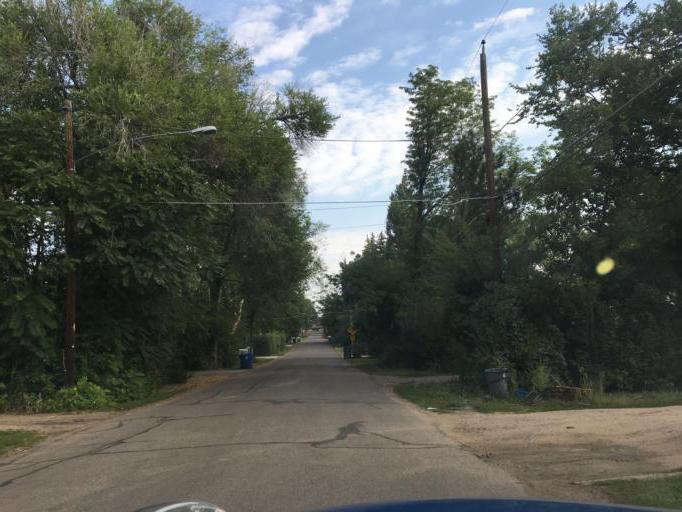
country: US
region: Colorado
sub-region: Jefferson County
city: Wheat Ridge
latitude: 39.7439
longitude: -105.1037
